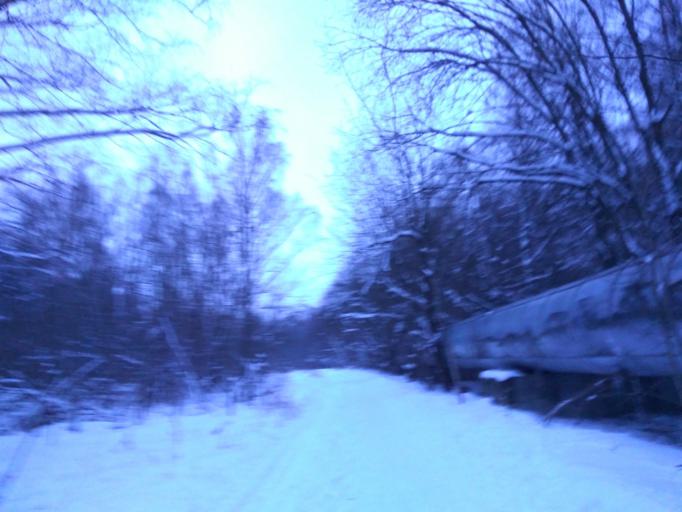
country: RU
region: Moscow
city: Biryulevo
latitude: 55.5897
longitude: 37.6987
